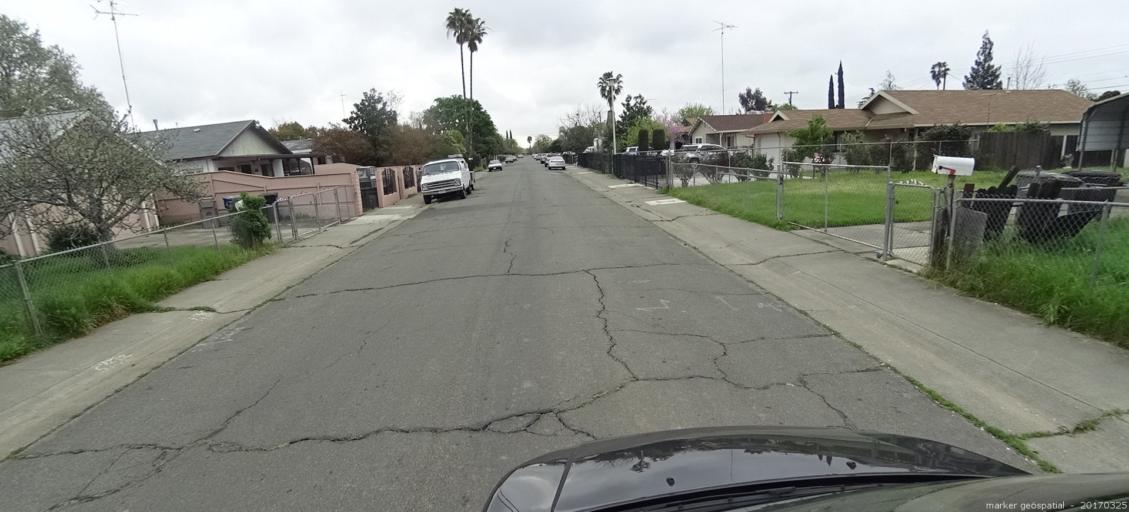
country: US
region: California
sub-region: Sacramento County
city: Florin
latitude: 38.5197
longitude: -121.4141
